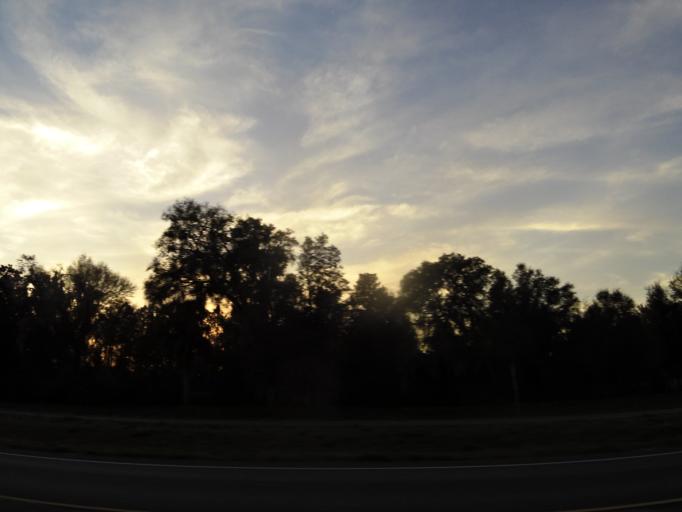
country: US
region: Florida
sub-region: Volusia County
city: North DeLand
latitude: 29.1037
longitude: -81.2950
